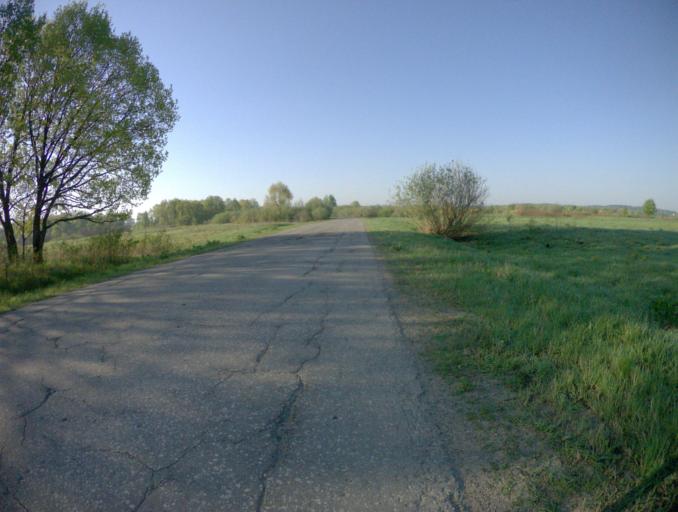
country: RU
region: Vladimir
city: Vyazniki
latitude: 56.2638
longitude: 42.1710
